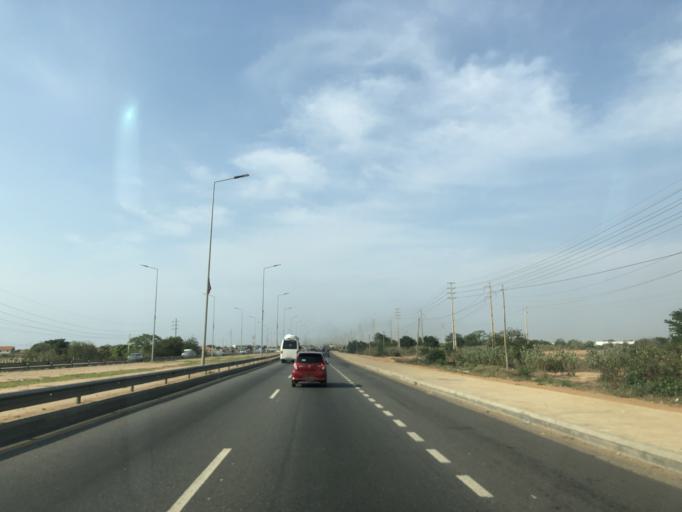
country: AO
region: Luanda
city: Luanda
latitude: -8.9502
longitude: 13.2596
